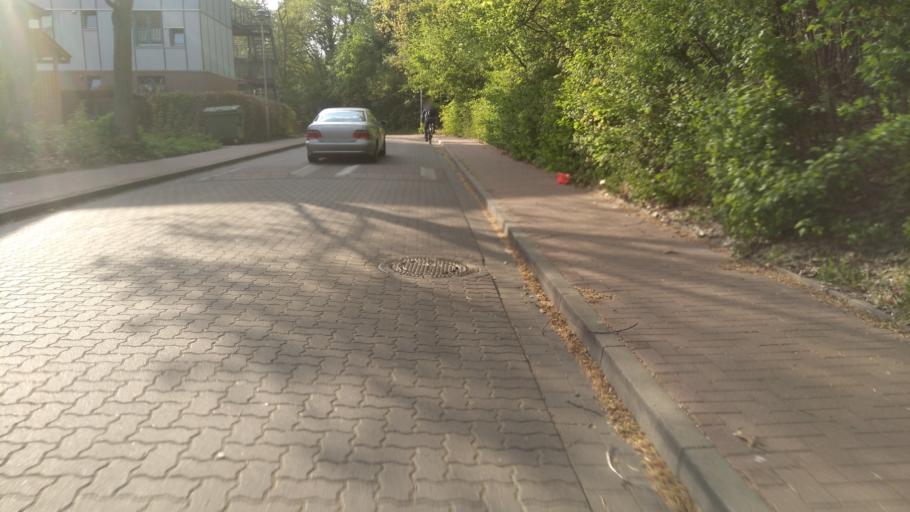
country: DE
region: Lower Saxony
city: Buxtehude
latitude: 53.4629
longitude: 9.6883
